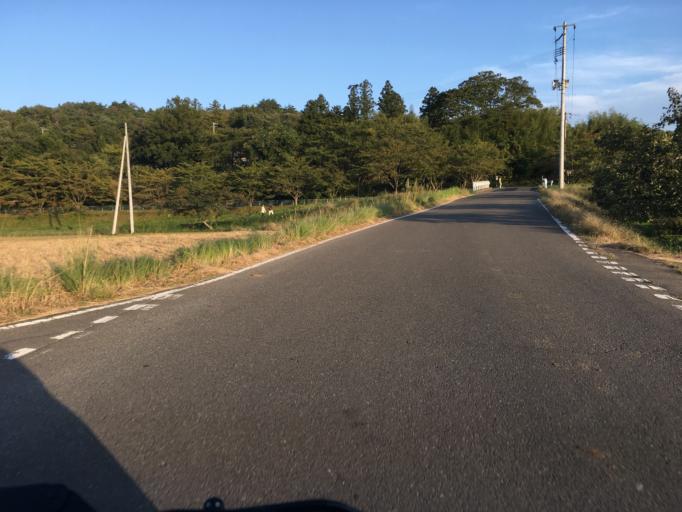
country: JP
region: Fukushima
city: Hobaramachi
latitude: 37.8106
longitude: 140.5766
